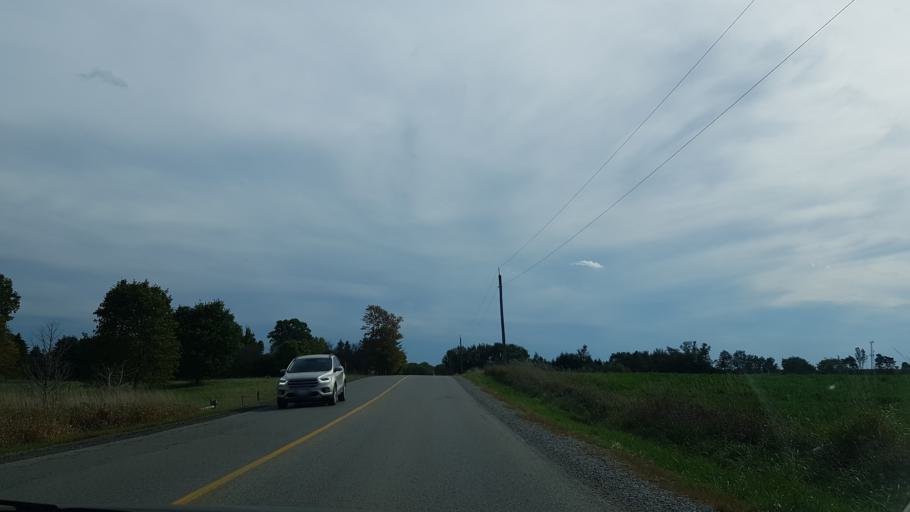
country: CA
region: Ontario
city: Delaware
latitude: 43.0144
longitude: -81.4033
